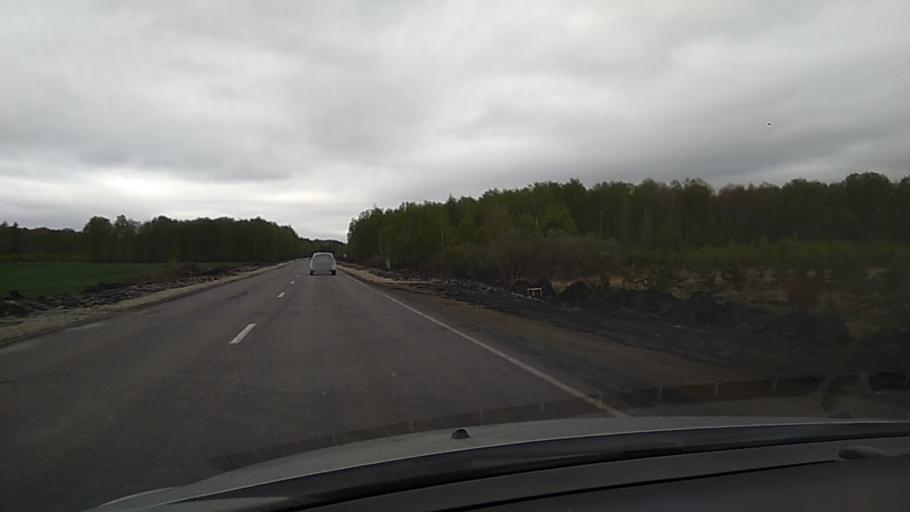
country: RU
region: Kurgan
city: Shadrinsk
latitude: 56.1417
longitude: 63.5249
